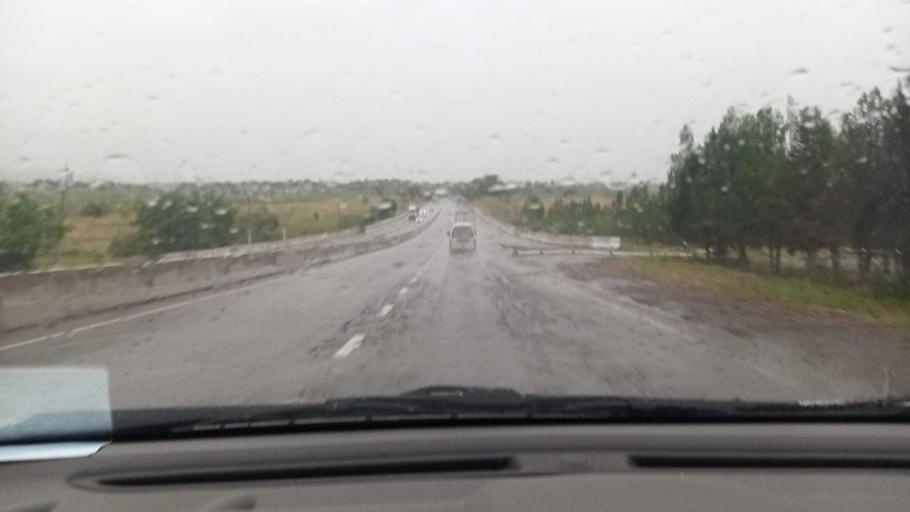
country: UZ
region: Toshkent
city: Angren
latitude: 40.9611
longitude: 69.9449
